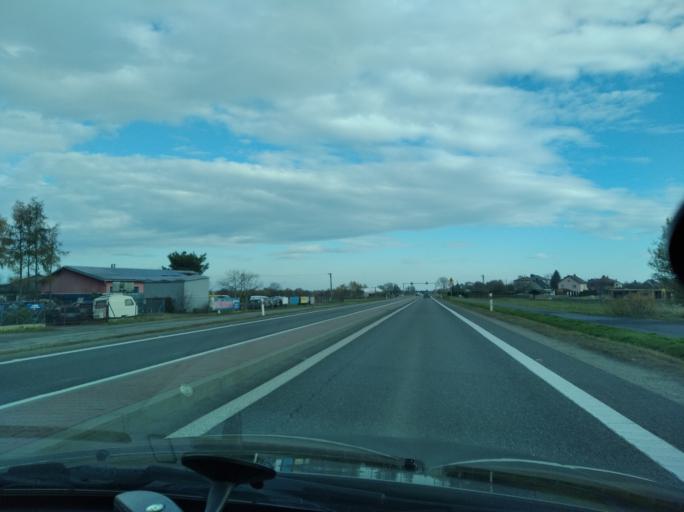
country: PL
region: Subcarpathian Voivodeship
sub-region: Powiat debicki
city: Debica
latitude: 50.0445
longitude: 21.4362
